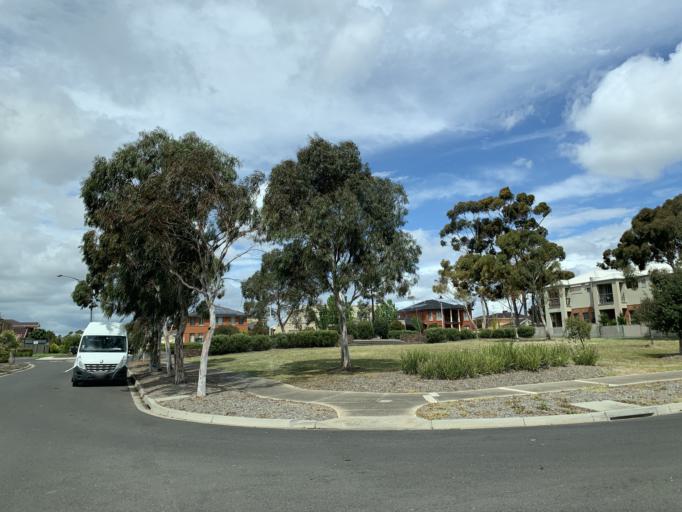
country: AU
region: Victoria
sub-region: Brimbank
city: Cairnlea
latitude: -37.7604
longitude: 144.7924
